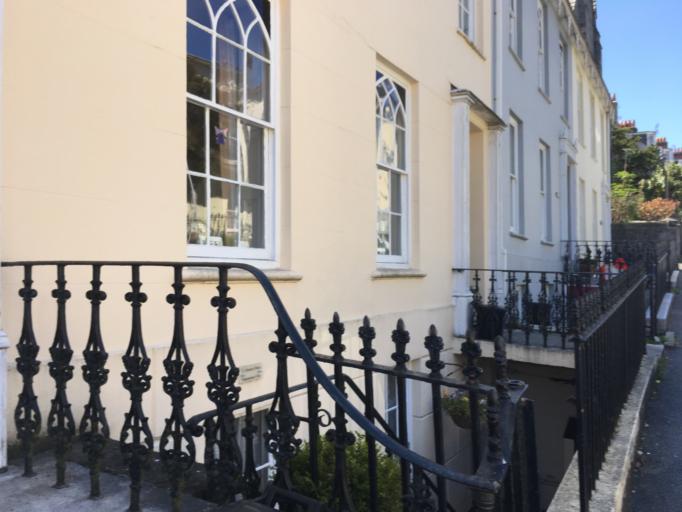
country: GG
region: St Peter Port
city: Saint Peter Port
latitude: 49.4541
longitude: -2.5451
